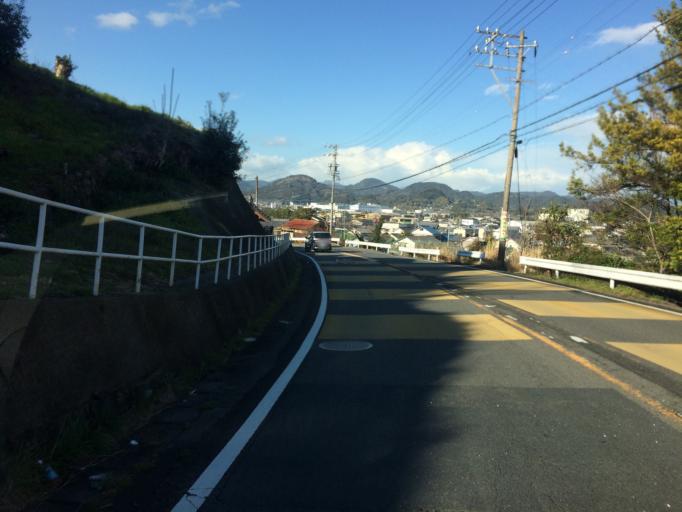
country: JP
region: Shizuoka
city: Kanaya
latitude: 34.8242
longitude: 138.1282
